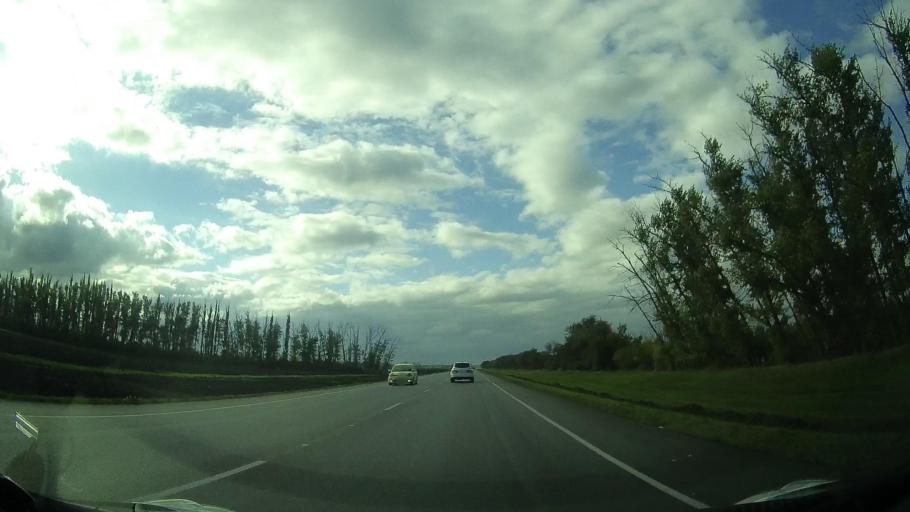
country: RU
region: Rostov
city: Tselina
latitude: 46.5314
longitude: 40.9394
